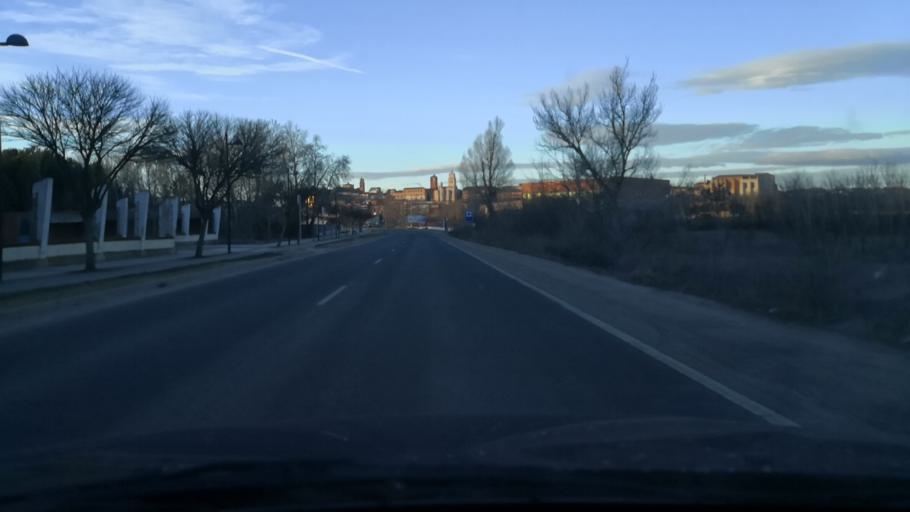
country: ES
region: Castille and Leon
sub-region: Provincia de Valladolid
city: Tordesillas
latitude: 41.4928
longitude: -4.9979
